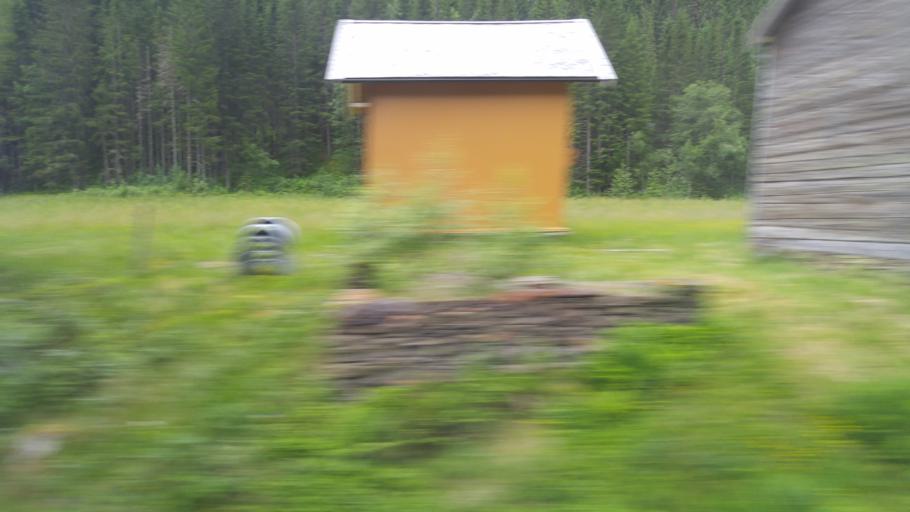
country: NO
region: Nord-Trondelag
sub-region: Meraker
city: Meraker
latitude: 63.4660
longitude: 11.4883
